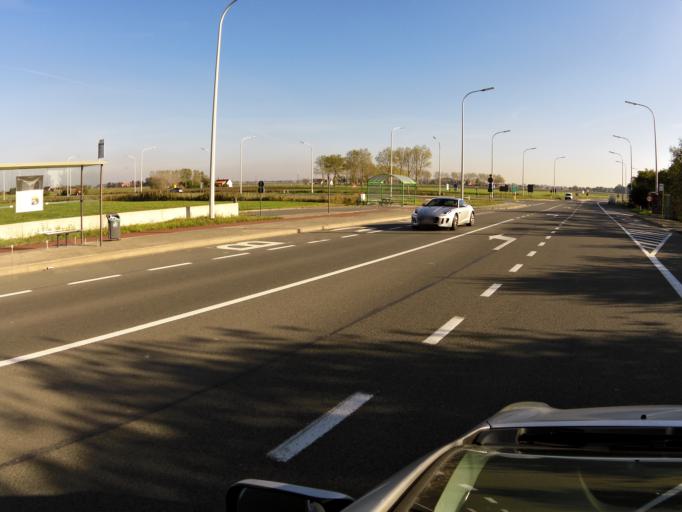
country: BE
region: Flanders
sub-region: Provincie West-Vlaanderen
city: Middelkerke
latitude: 51.1395
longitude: 2.8623
